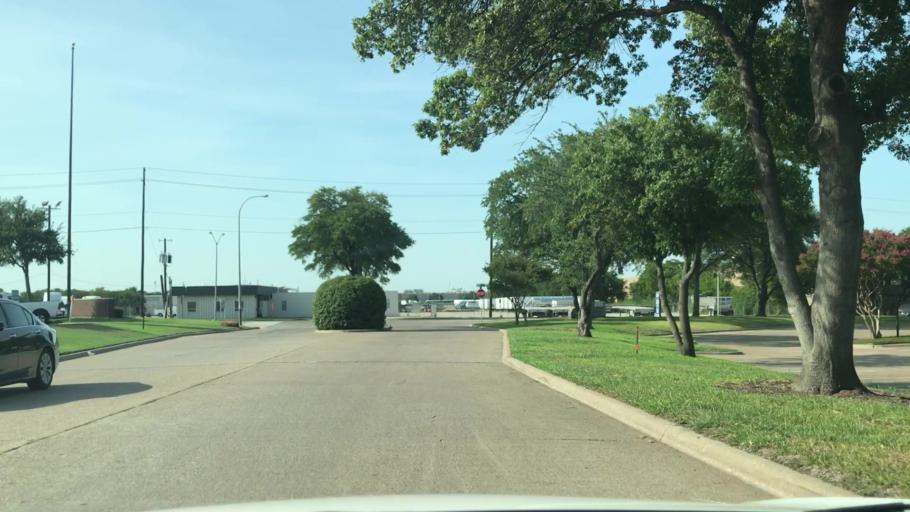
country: US
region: Texas
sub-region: Dallas County
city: Richardson
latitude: 32.8936
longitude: -96.7063
